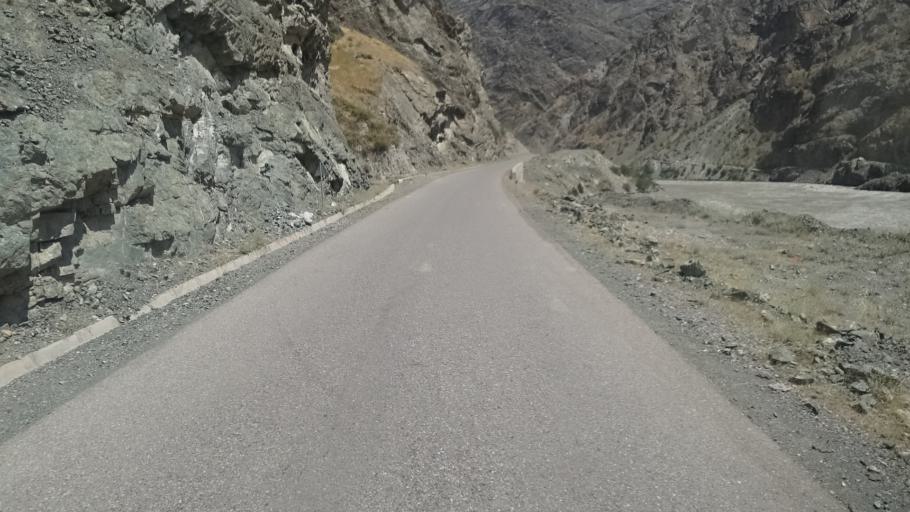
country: AF
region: Badakhshan
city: Deh Khwahan
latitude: 37.9878
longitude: 70.2913
